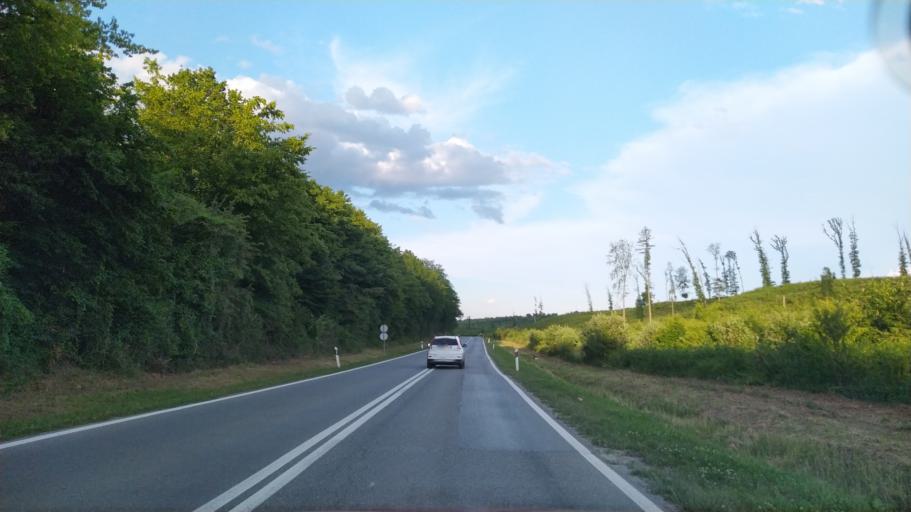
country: HR
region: Osjecko-Baranjska
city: Martin
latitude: 45.4902
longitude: 18.0368
